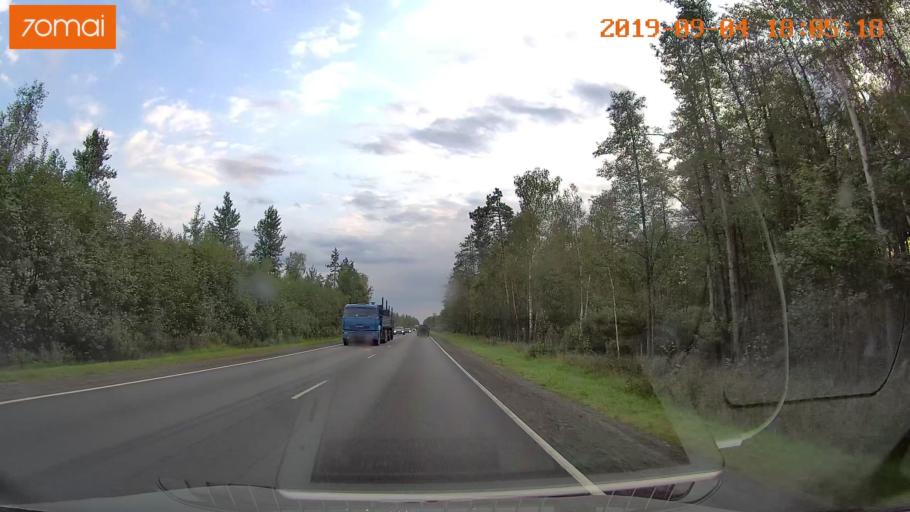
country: RU
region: Moskovskaya
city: Il'inskiy Pogost
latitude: 55.4429
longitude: 38.8283
